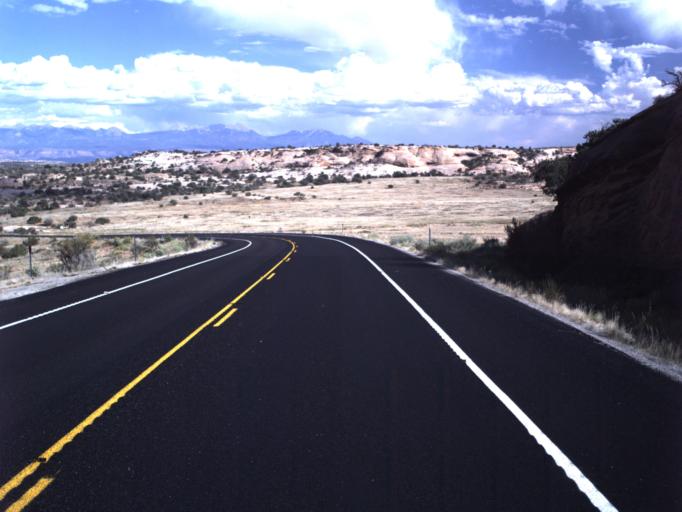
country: US
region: Utah
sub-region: Grand County
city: Moab
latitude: 38.6361
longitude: -109.7833
